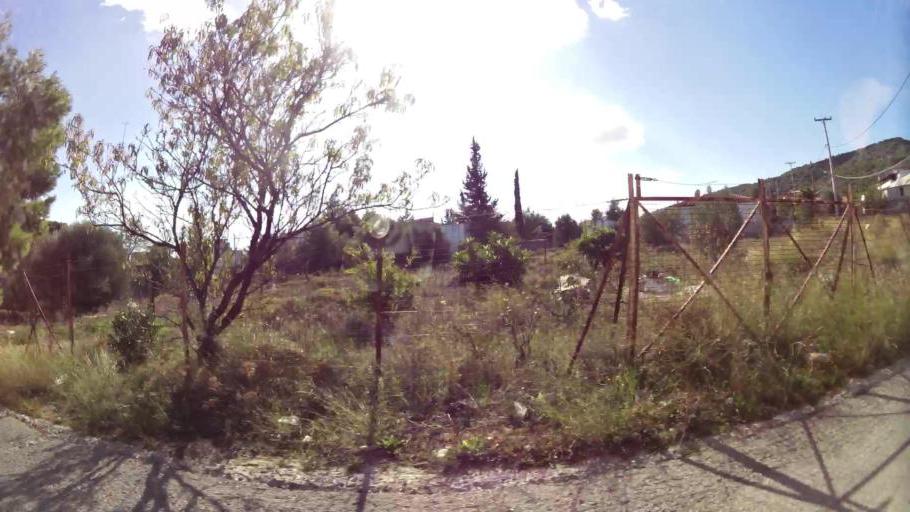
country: GR
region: Attica
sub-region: Nomarchia Anatolikis Attikis
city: Thrakomakedones
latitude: 38.1158
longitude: 23.7282
